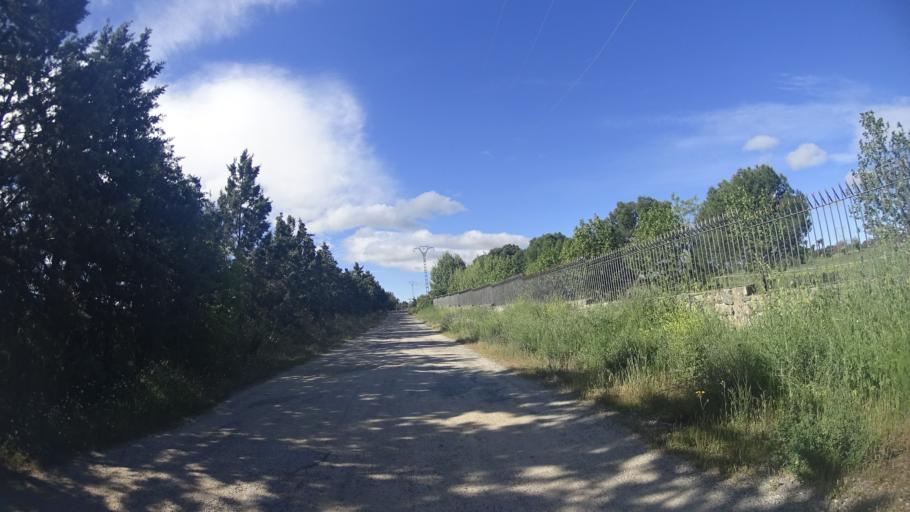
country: ES
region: Madrid
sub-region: Provincia de Madrid
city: Villanueva del Pardillo
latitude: 40.4978
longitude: -3.9404
